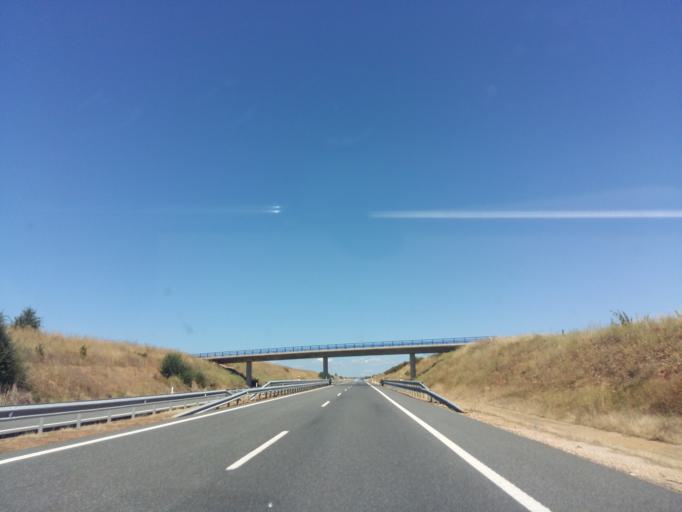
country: ES
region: Castille and Leon
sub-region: Provincia de Leon
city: Bustillo del Paramo
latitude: 42.4856
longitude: -5.8059
